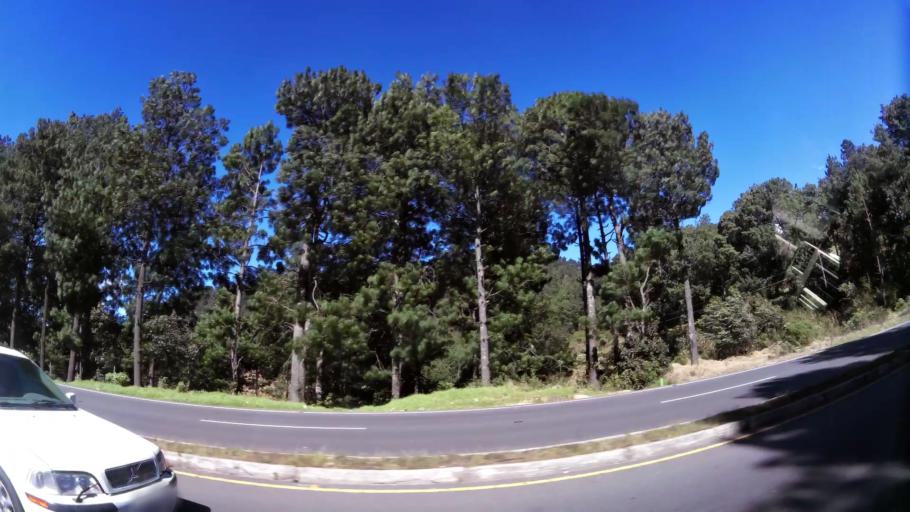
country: GT
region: Solola
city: Solola
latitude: 14.8204
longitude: -91.2011
